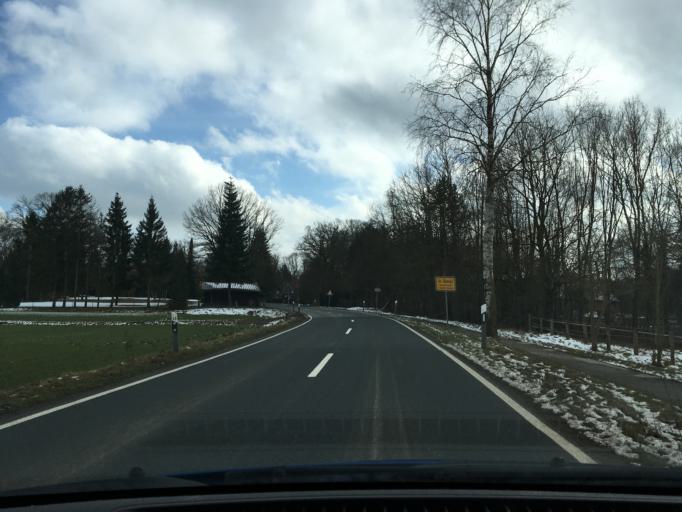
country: DE
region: Lower Saxony
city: Barum
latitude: 53.3370
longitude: 10.3973
